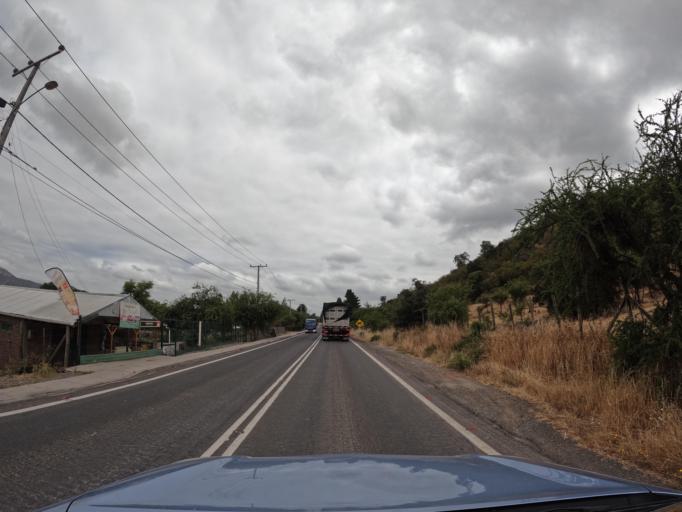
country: CL
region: Maule
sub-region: Provincia de Curico
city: Teno
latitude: -34.8005
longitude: -71.2240
